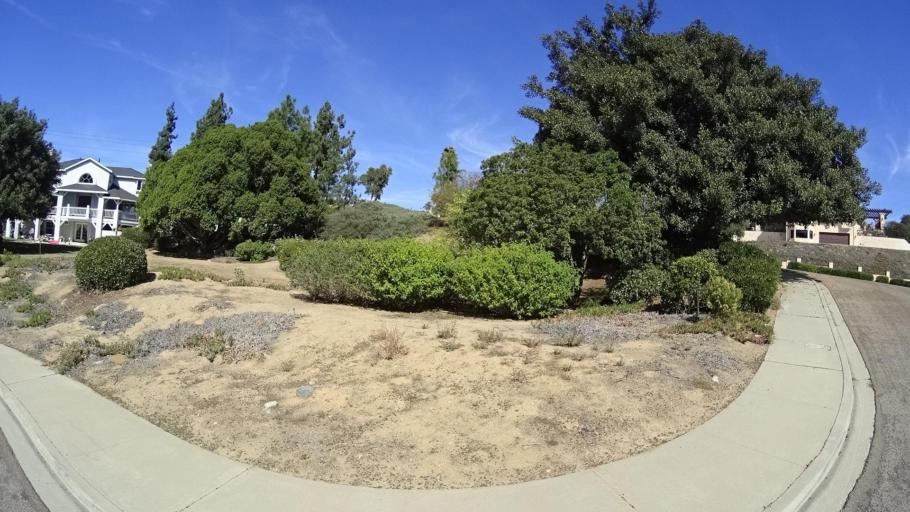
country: US
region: California
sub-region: San Diego County
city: Casa de Oro-Mount Helix
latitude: 32.7558
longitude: -116.9525
